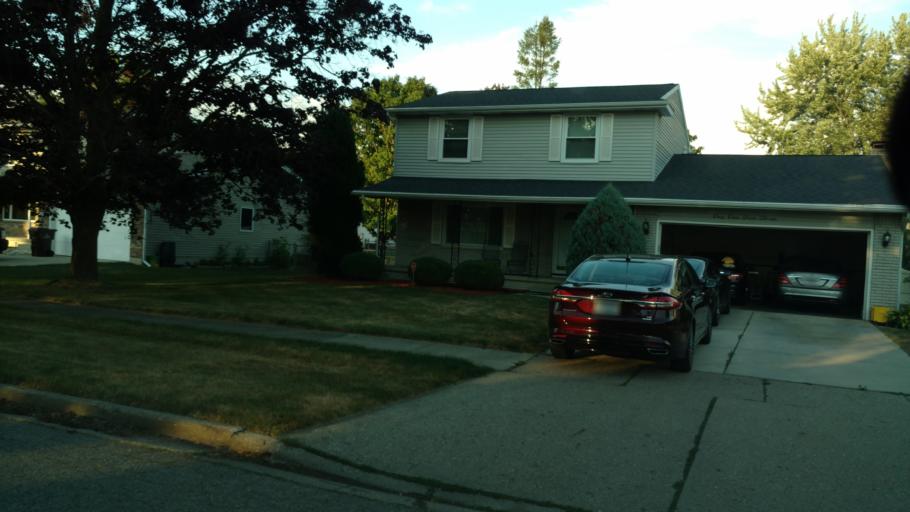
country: US
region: Michigan
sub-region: Eaton County
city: Waverly
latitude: 42.7206
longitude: -84.6294
